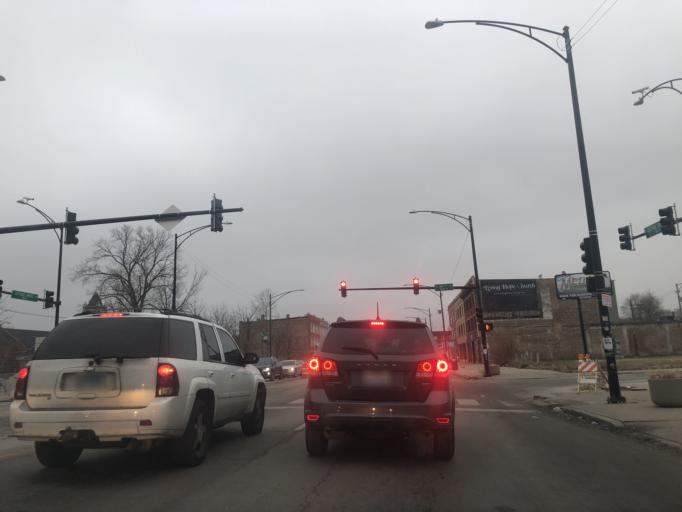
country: US
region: Illinois
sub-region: Cook County
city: Chicago
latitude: 41.7789
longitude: -87.6060
